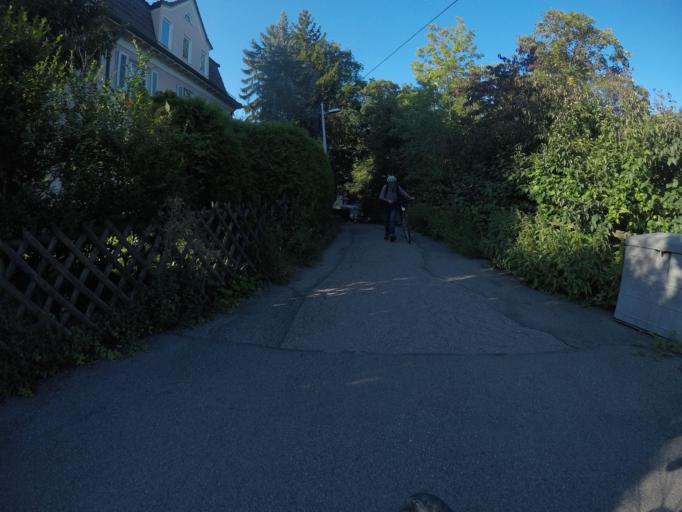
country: DE
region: Baden-Wuerttemberg
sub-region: Regierungsbezirk Stuttgart
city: Stuttgart Feuerbach
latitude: 48.7758
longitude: 9.1398
